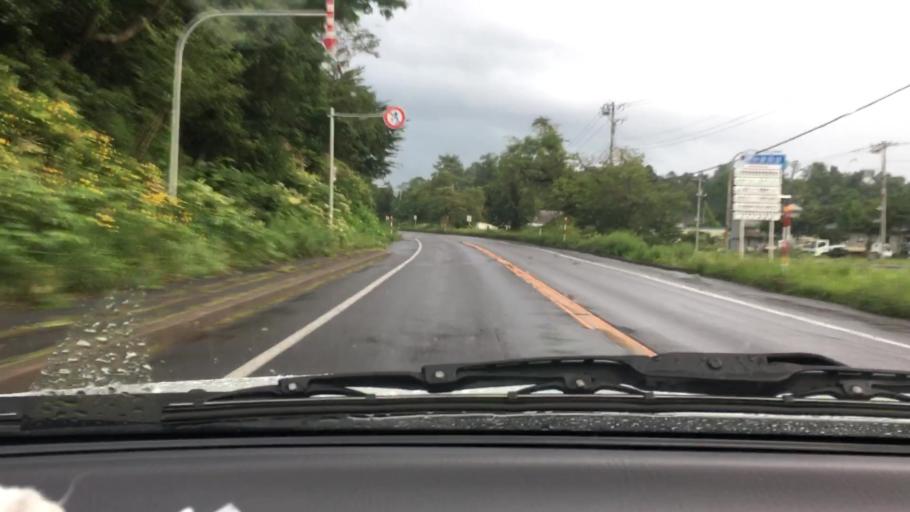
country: JP
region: Hokkaido
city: Nanae
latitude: 42.0837
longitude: 140.5859
